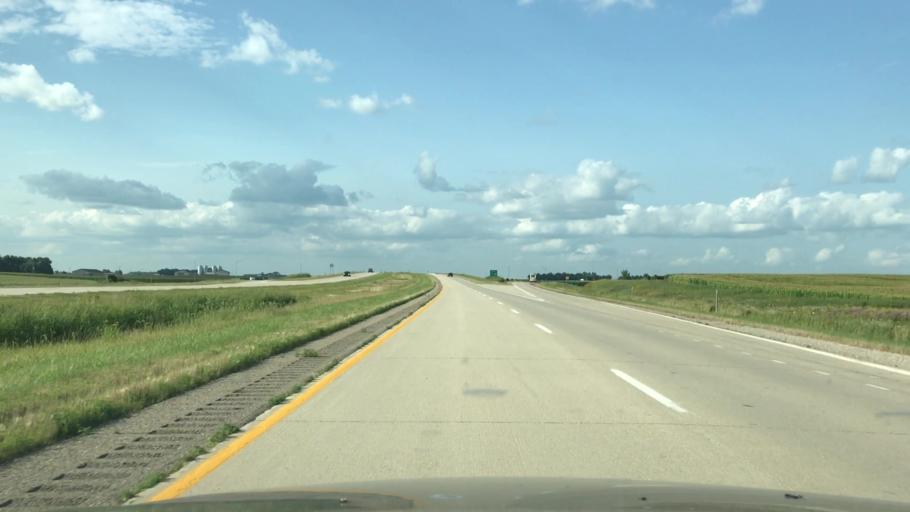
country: US
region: Iowa
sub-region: Osceola County
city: Sibley
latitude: 43.4272
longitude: -95.7142
